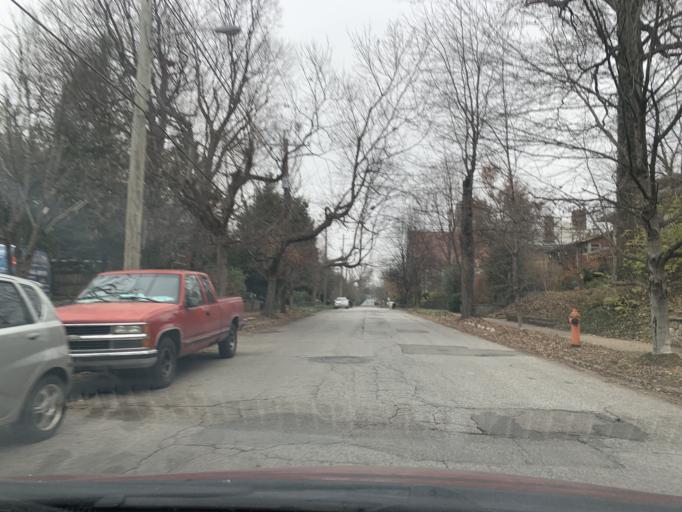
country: US
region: Kentucky
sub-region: Jefferson County
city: Indian Hills
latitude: 38.2516
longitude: -85.6976
